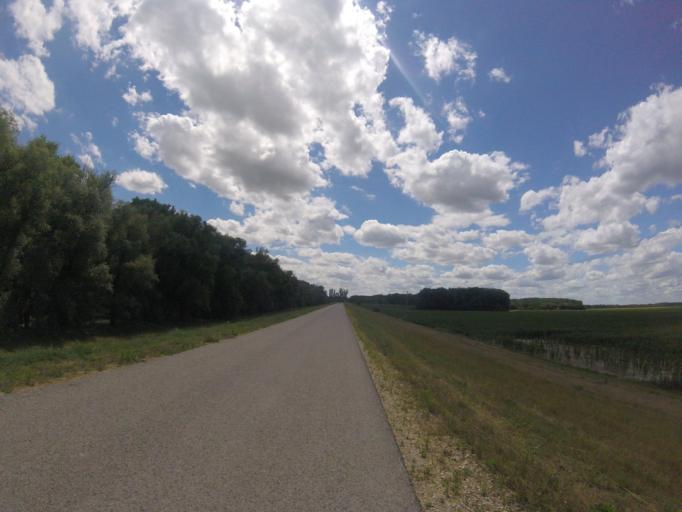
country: HU
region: Tolna
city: Bogyiszlo
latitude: 46.4185
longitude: 18.8876
